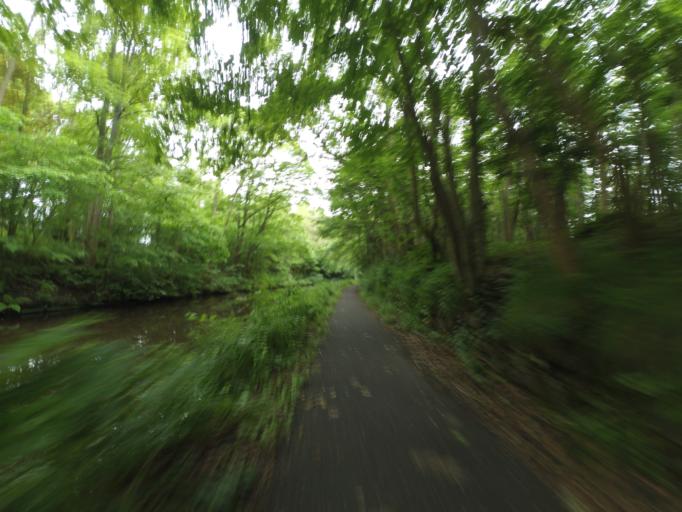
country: GB
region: Scotland
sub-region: West Lothian
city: Broxburn
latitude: 55.9702
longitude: -3.4801
